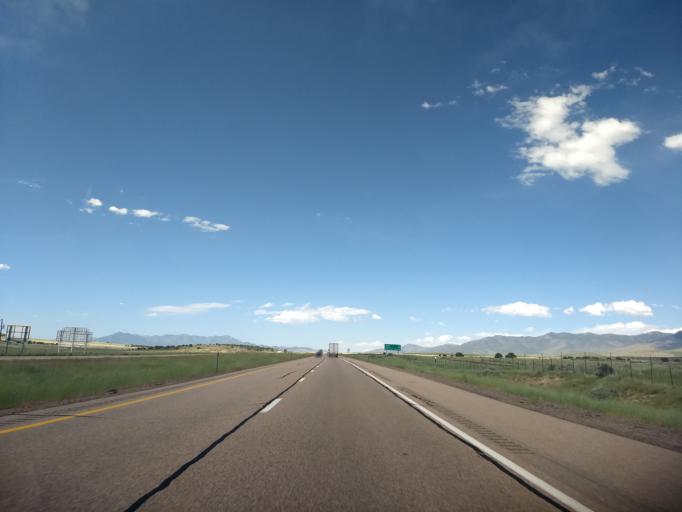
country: US
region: Utah
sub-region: Millard County
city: Fillmore
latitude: 39.0032
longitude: -112.3138
